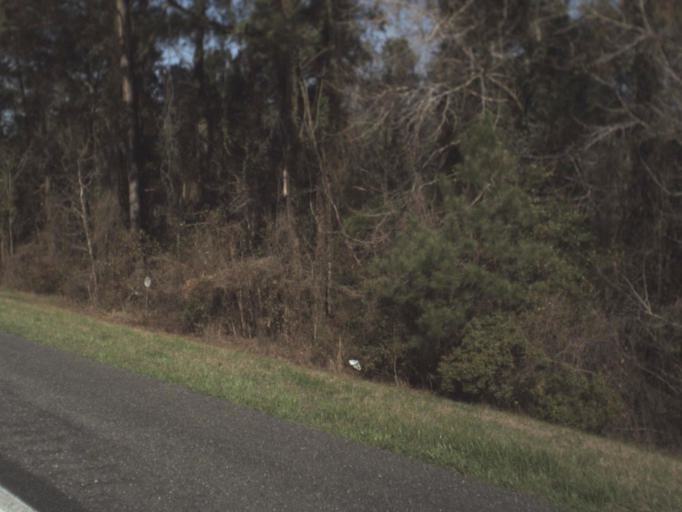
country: US
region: Florida
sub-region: Jefferson County
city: Monticello
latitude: 30.4786
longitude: -83.9268
